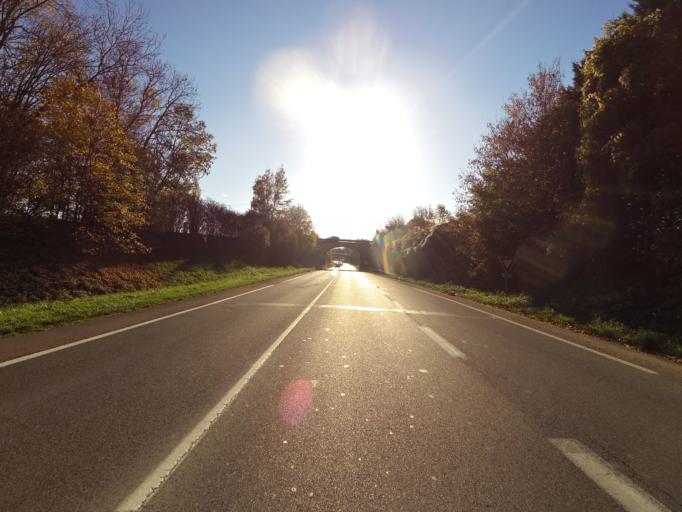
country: FR
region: Champagne-Ardenne
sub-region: Departement de l'Aube
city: Breviandes
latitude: 48.2601
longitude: 4.0962
